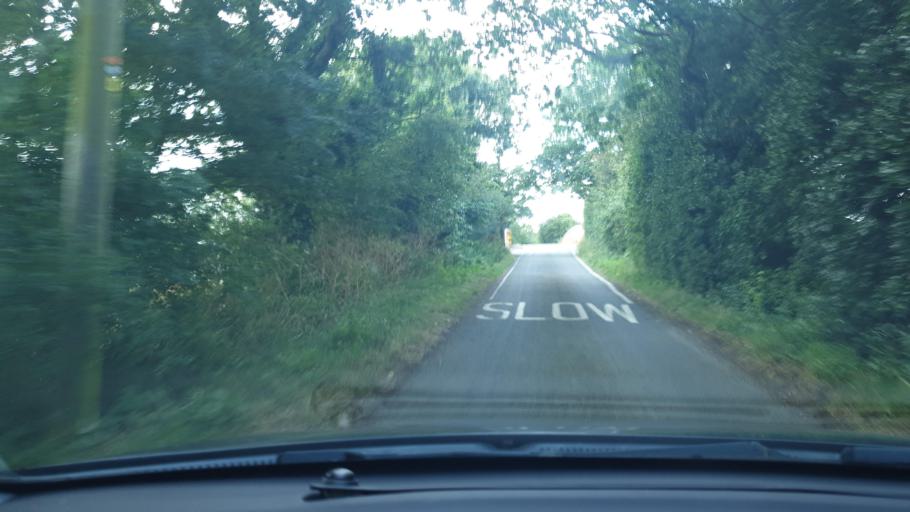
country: GB
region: England
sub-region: Suffolk
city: East Bergholt
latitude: 51.9252
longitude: 0.9938
